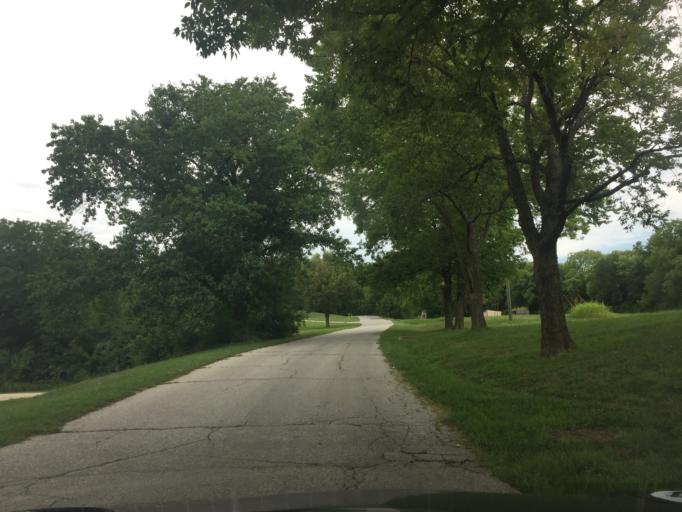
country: US
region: Missouri
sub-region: Platte County
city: Weston
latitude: 39.3679
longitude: -94.9209
